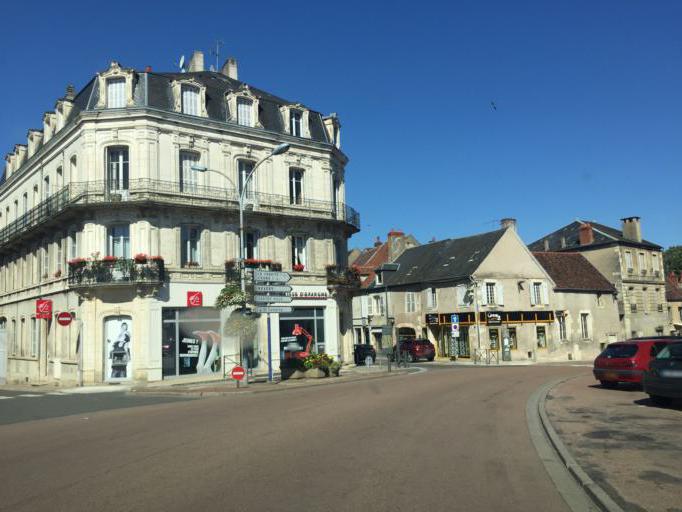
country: FR
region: Bourgogne
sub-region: Departement de la Nievre
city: Clamecy
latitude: 47.4599
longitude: 3.5230
